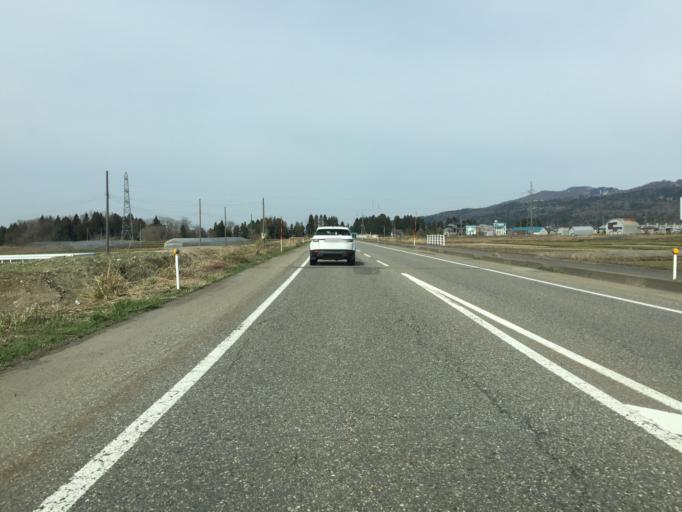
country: JP
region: Niigata
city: Ojiya
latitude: 37.3399
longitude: 138.8139
